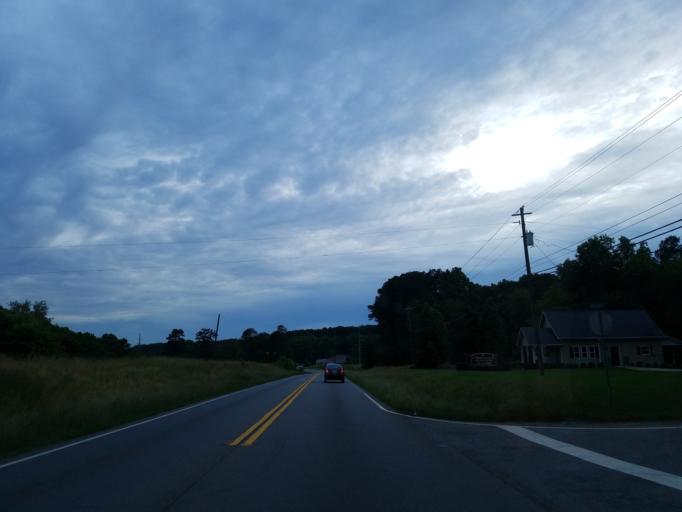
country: US
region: Georgia
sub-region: Cherokee County
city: Ball Ground
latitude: 34.2414
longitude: -84.3877
